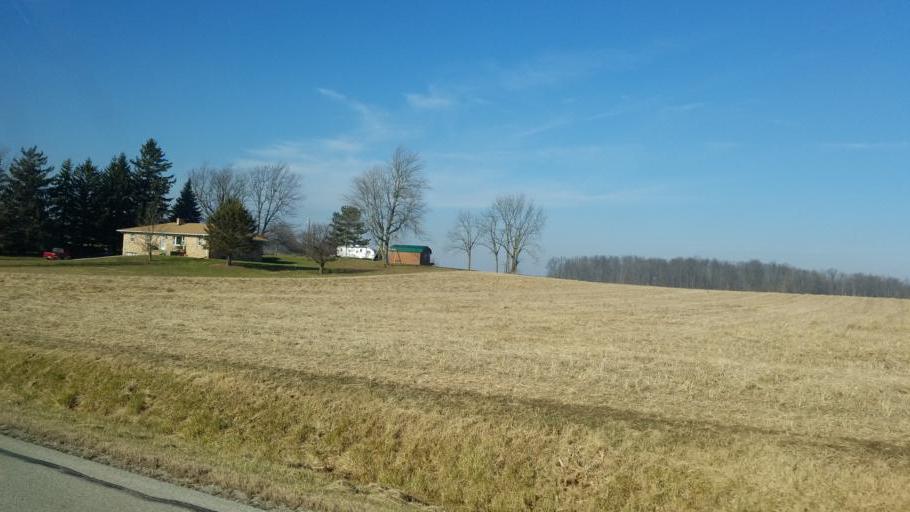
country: US
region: Ohio
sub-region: Crawford County
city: Bucyrus
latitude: 40.9067
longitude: -83.0235
